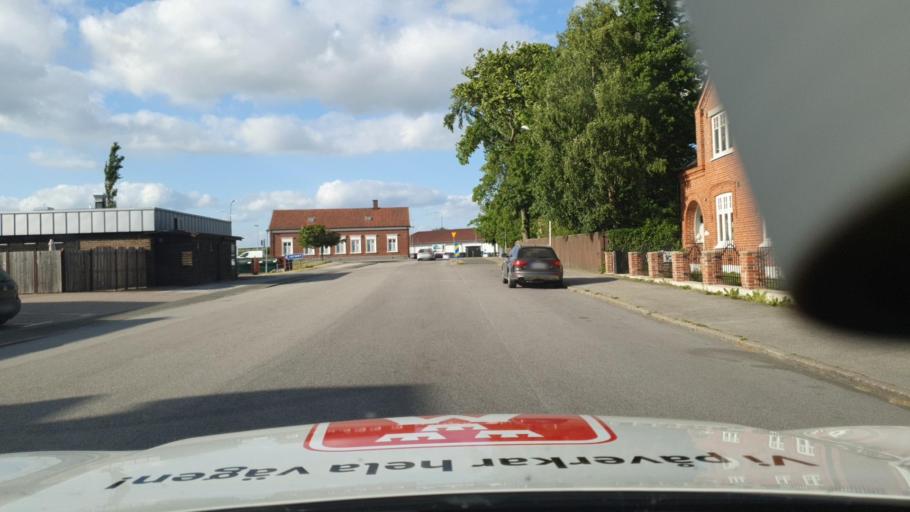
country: SE
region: Skane
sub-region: Tomelilla Kommun
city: Tomelilla
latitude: 55.5456
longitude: 13.9464
